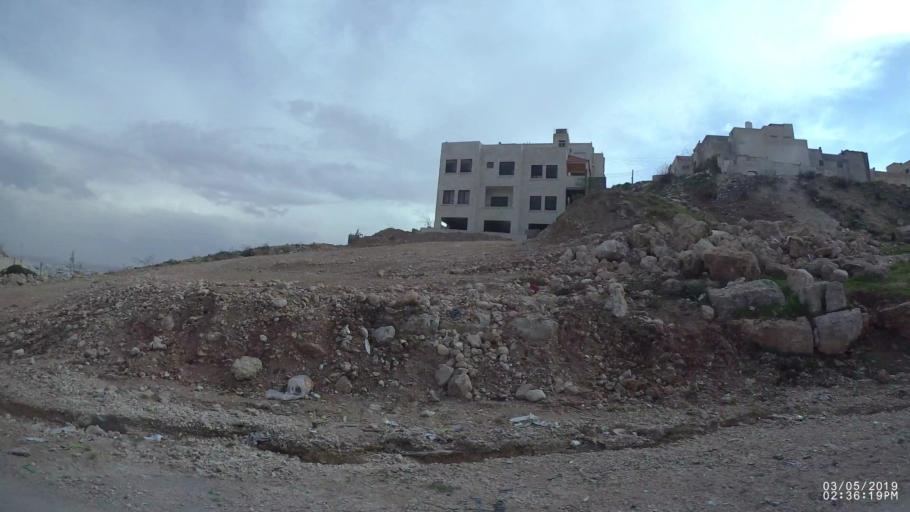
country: JO
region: Amman
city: Amman
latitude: 32.0150
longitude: 35.9445
